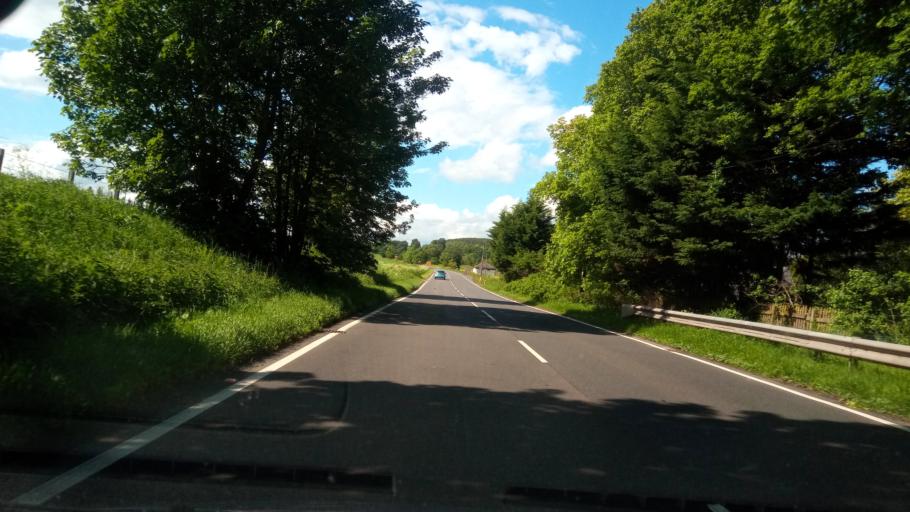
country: GB
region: Scotland
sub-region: The Scottish Borders
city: Jedburgh
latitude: 55.4284
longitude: -2.5312
